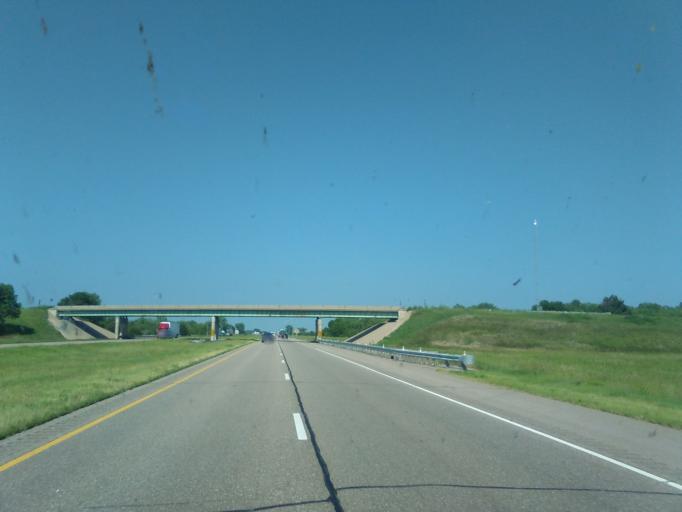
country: US
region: Nebraska
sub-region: Buffalo County
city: Gibbon
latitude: 40.7015
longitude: -98.8470
